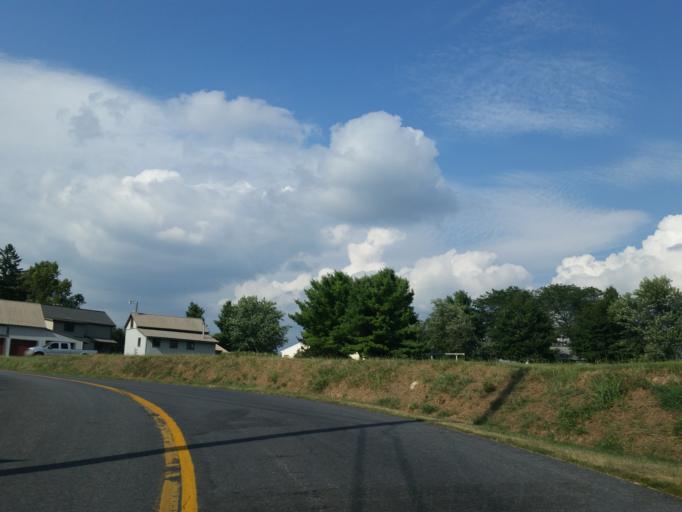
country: US
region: Pennsylvania
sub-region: Lancaster County
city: Manheim
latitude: 40.1703
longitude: -76.4554
